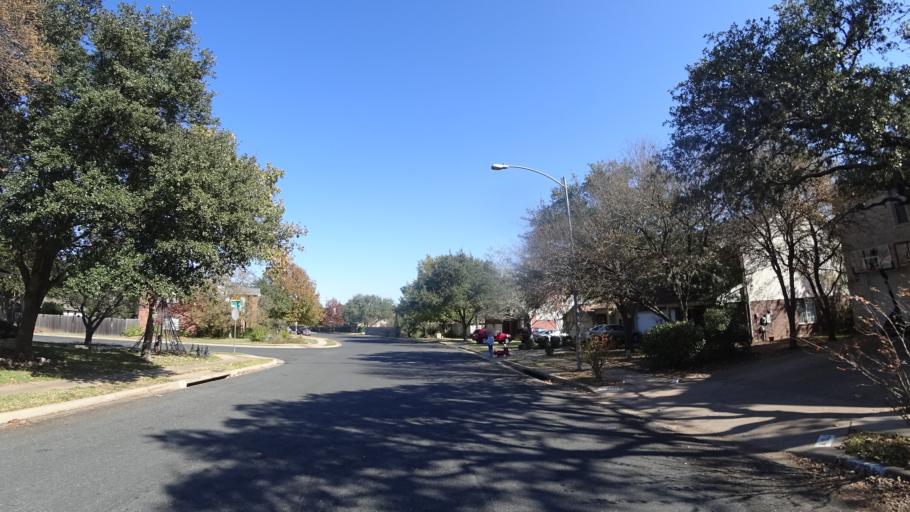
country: US
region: Texas
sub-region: Travis County
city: Barton Creek
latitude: 30.2265
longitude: -97.8633
